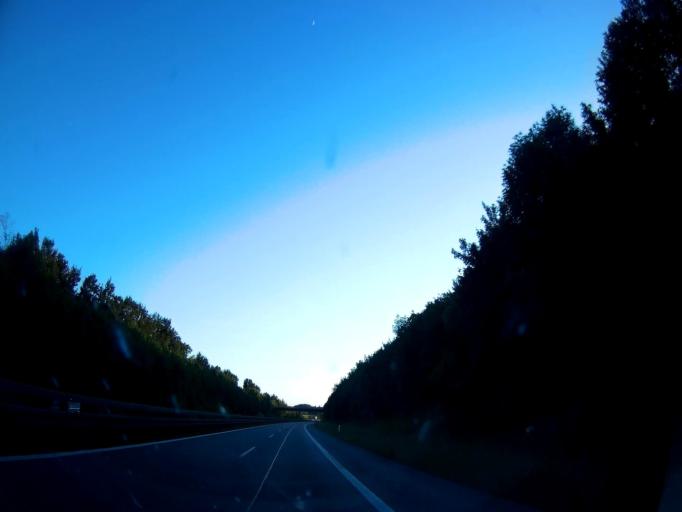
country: DE
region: Baden-Wuerttemberg
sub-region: Regierungsbezirk Stuttgart
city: Wallhausen
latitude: 49.1761
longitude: 10.0275
